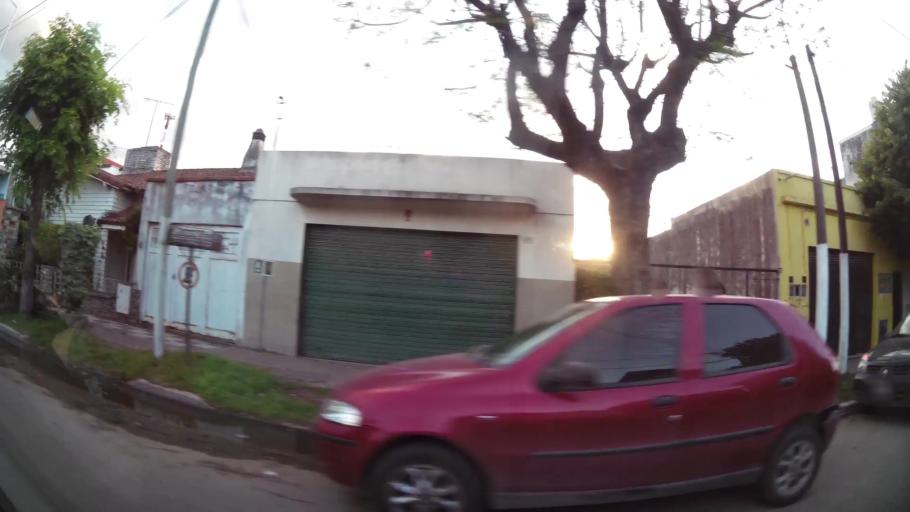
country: AR
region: Buenos Aires
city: Santa Catalina - Dique Lujan
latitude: -34.4718
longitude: -58.7602
